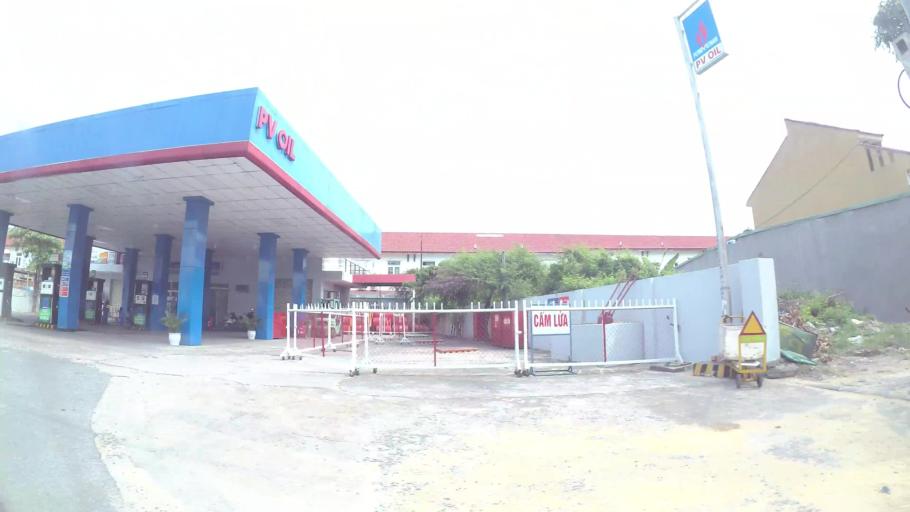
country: VN
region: Da Nang
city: Da Nang
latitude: 16.0817
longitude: 108.2361
